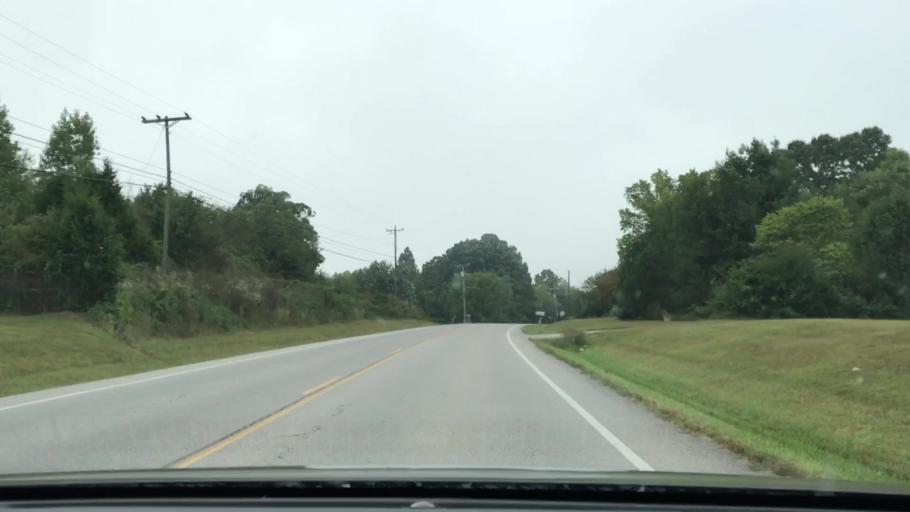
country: US
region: Tennessee
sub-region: Sumner County
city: Portland
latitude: 36.4977
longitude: -86.4973
